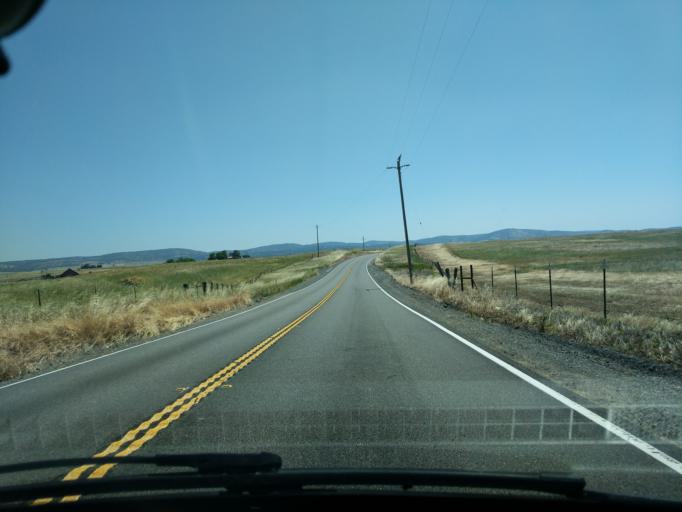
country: US
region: California
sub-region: Stanislaus County
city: East Oakdale
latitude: 37.9448
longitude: -120.8279
